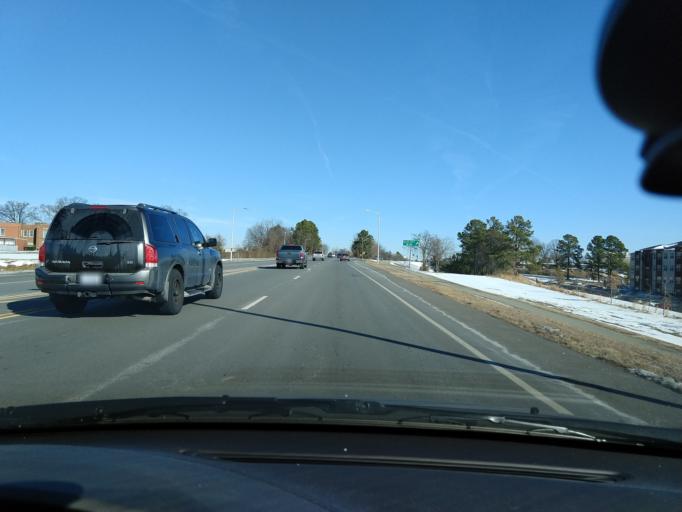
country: US
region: North Carolina
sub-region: Guilford County
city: Greensboro
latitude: 36.0613
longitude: -79.8003
